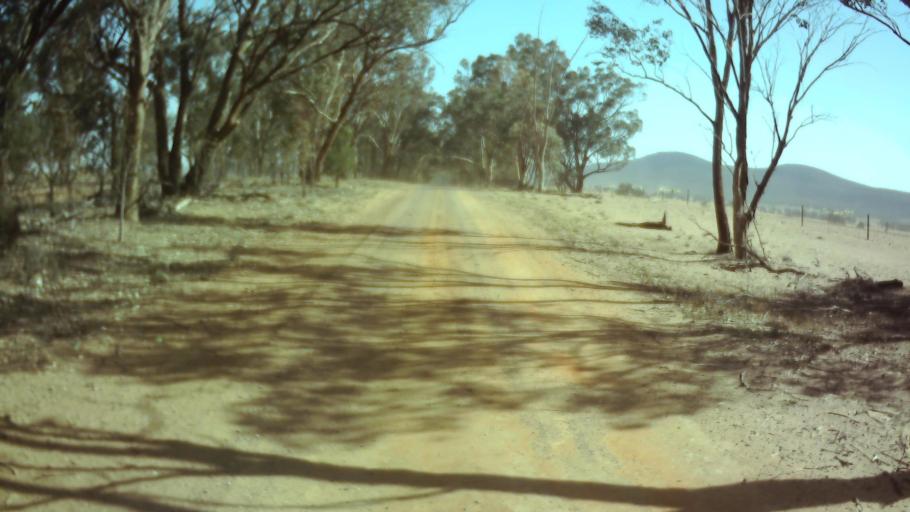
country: AU
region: New South Wales
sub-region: Weddin
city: Grenfell
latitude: -33.8478
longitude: 148.0169
